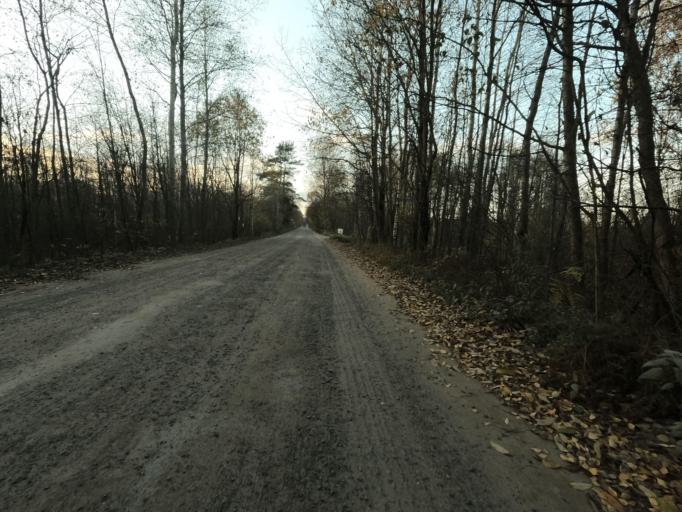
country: RU
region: Leningrad
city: Mga
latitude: 59.7628
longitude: 31.2542
